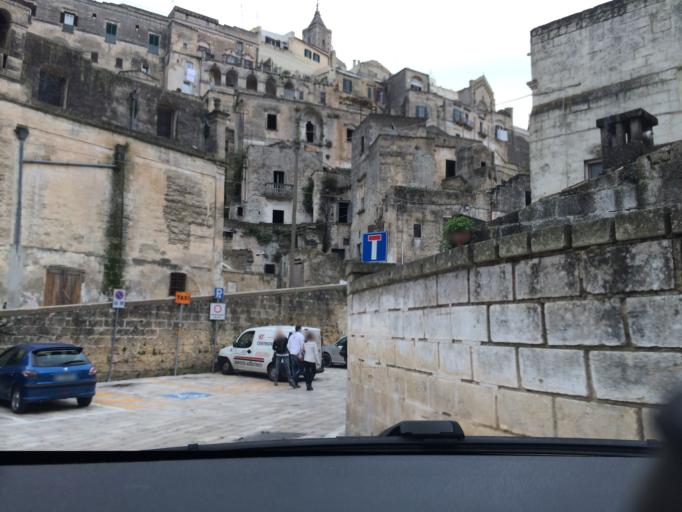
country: IT
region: Basilicate
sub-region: Provincia di Matera
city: Matera
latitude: 40.6677
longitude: 16.6103
